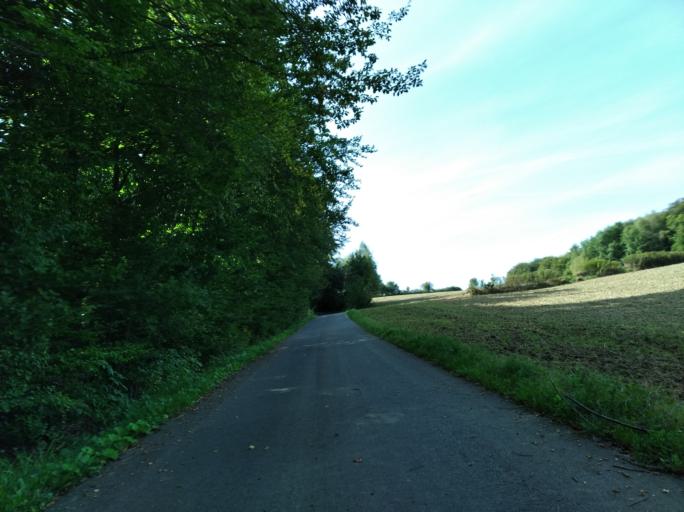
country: PL
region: Subcarpathian Voivodeship
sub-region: Powiat strzyzowski
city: Wisniowa
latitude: 49.8892
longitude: 21.6365
